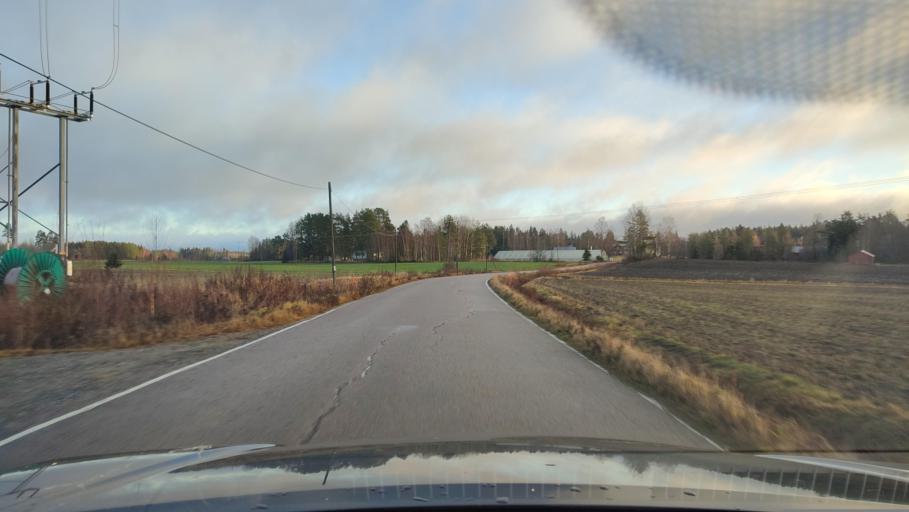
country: FI
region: Ostrobothnia
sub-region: Sydosterbotten
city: Naerpes
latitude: 62.4426
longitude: 21.3723
